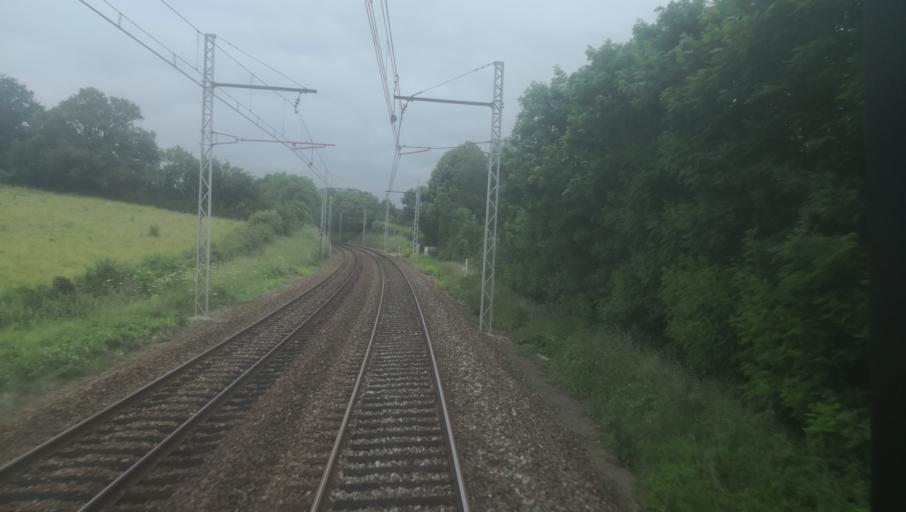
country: FR
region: Centre
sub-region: Departement de l'Indre
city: Le Pechereau
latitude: 46.5442
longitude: 1.5417
